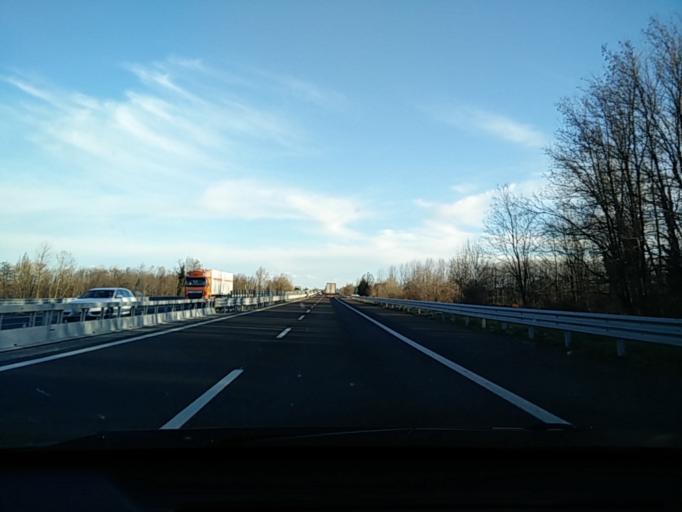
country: IT
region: Friuli Venezia Giulia
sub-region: Provincia di Udine
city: Buia
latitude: 46.1999
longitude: 13.0996
